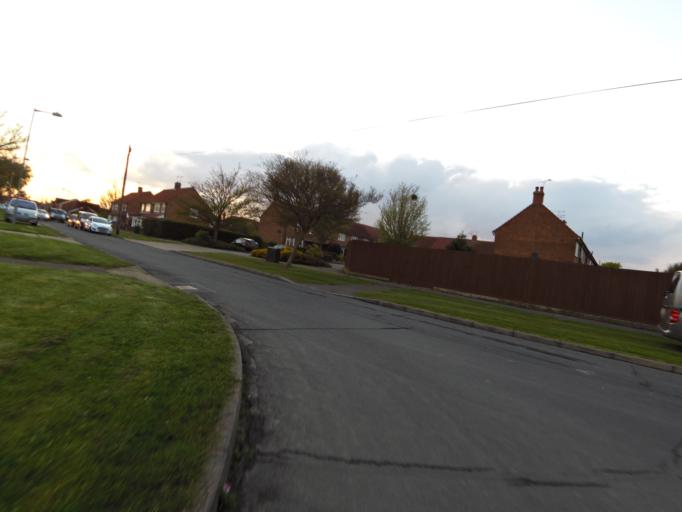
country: GB
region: England
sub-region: Suffolk
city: Kesgrave
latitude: 52.0694
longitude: 1.1958
